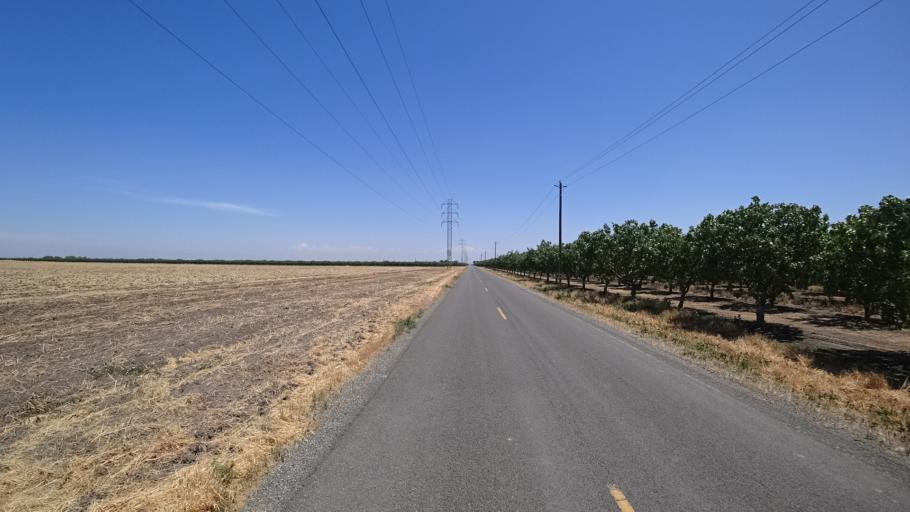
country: US
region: California
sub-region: Kings County
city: Corcoran
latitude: 36.1090
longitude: -119.5485
